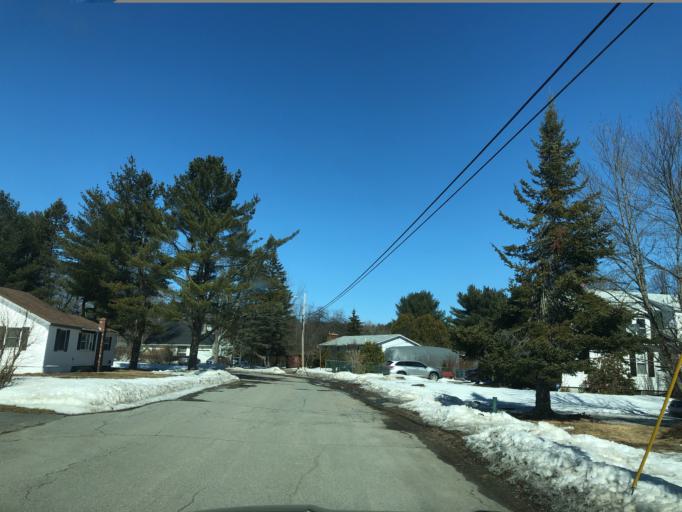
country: US
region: Maine
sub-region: Penobscot County
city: Brewer
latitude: 44.8197
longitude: -68.7545
